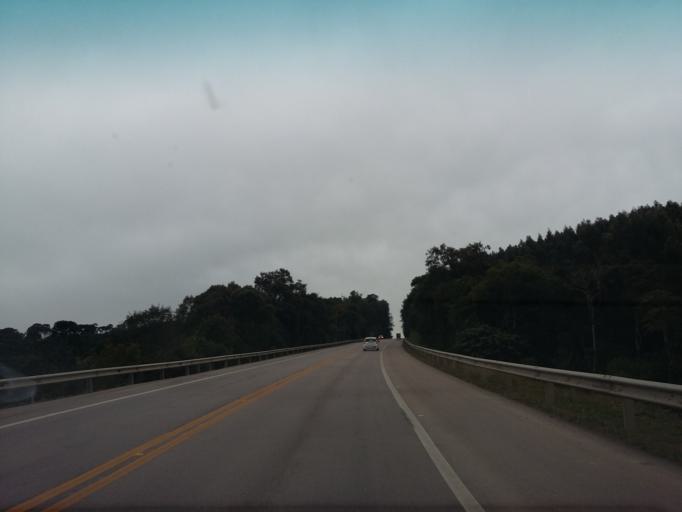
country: BR
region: Santa Catarina
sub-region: Santa Cecilia
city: Santa Cecilia
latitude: -26.6837
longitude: -50.2934
